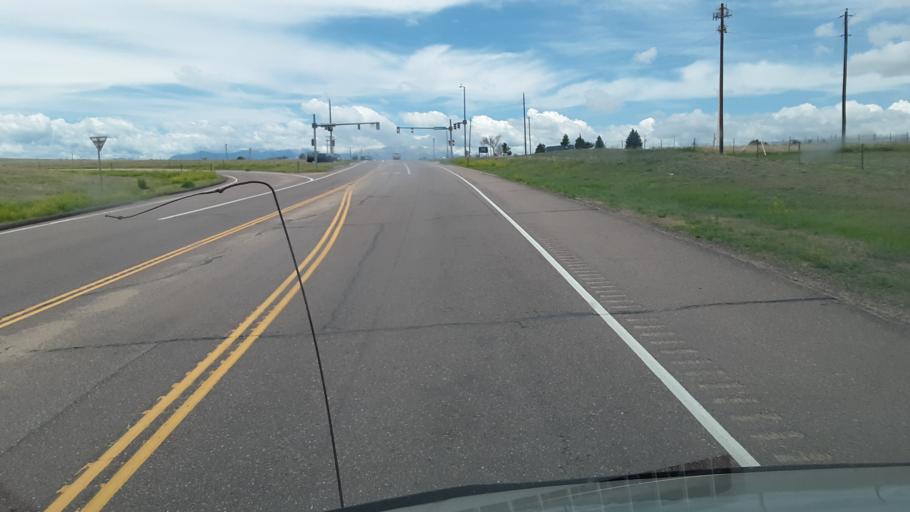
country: US
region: Colorado
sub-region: El Paso County
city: Ellicott
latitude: 38.8387
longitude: -104.5332
